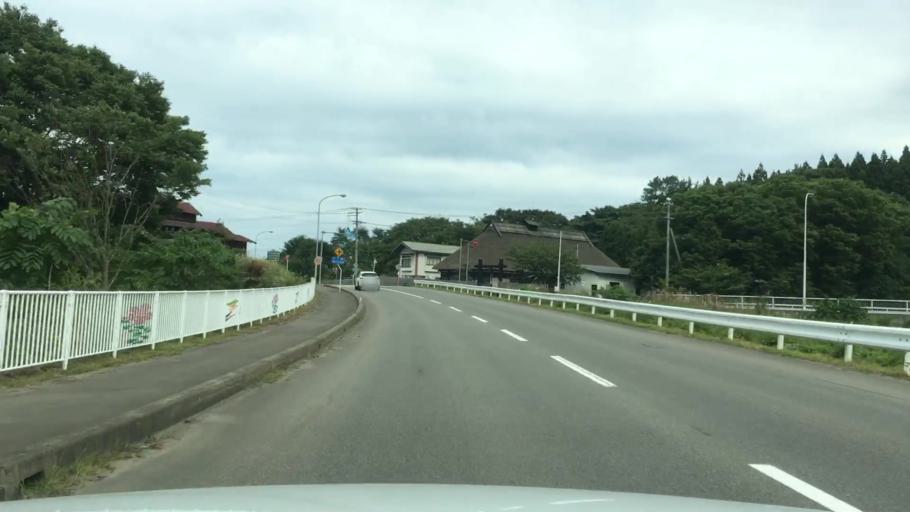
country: JP
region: Aomori
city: Shimokizukuri
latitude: 40.7570
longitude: 140.2307
